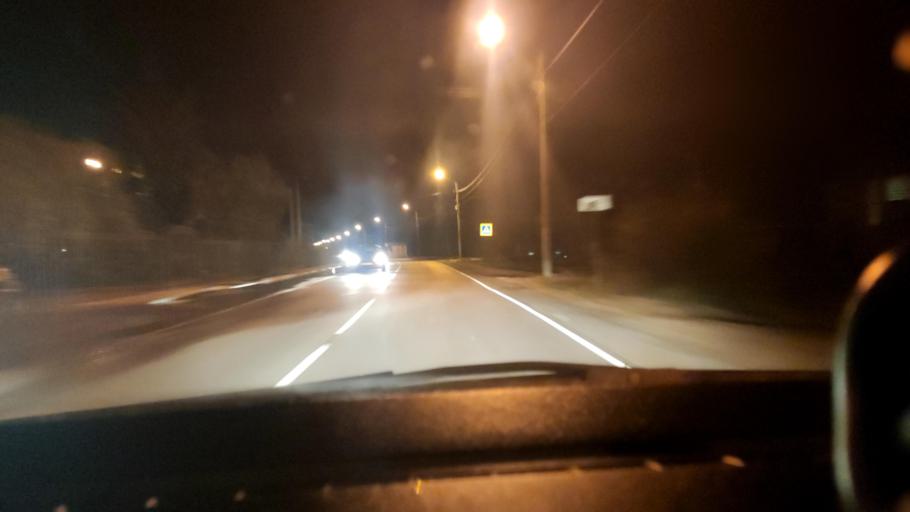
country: RU
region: Voronezj
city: Shilovo
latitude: 51.5669
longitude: 39.0484
